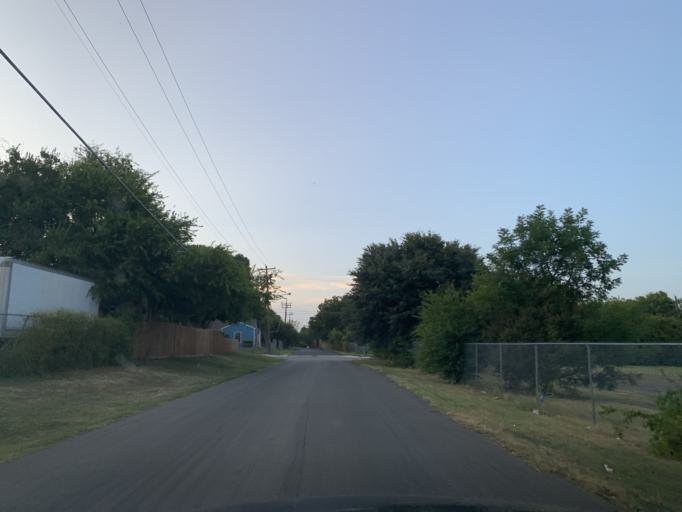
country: US
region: Texas
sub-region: Dallas County
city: Dallas
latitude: 32.6952
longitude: -96.8003
